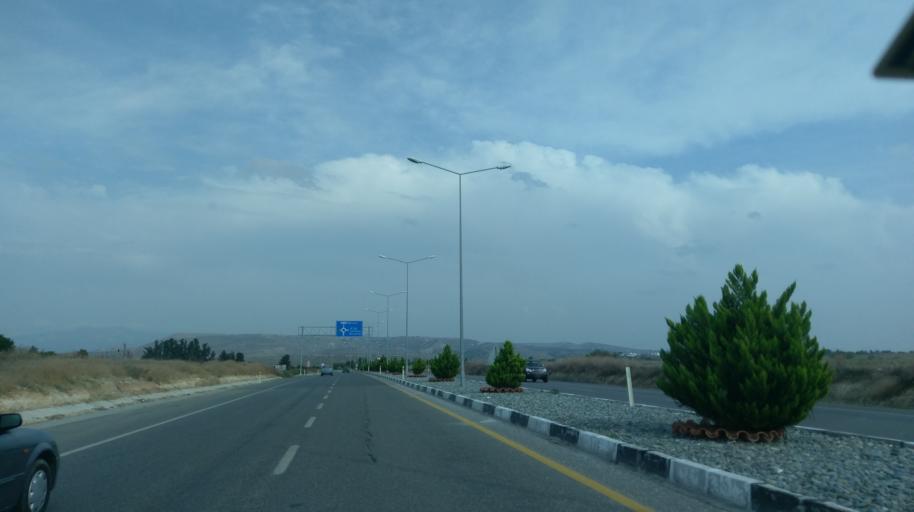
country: CY
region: Lefkosia
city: Morfou
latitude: 35.2037
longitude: 33.0399
